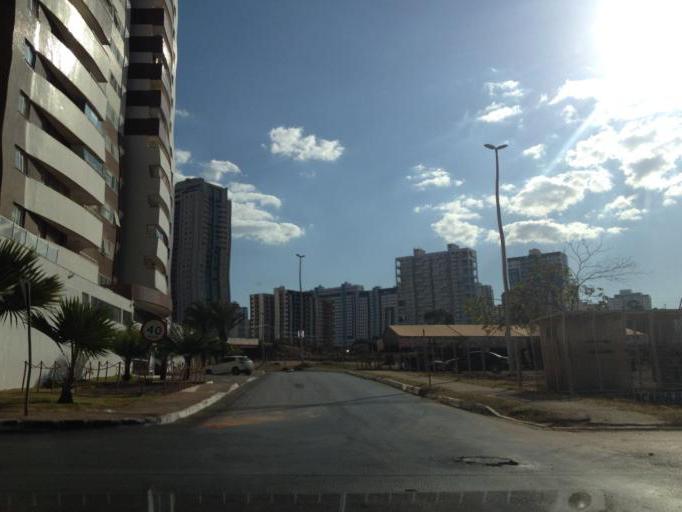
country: BR
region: Federal District
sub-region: Brasilia
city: Brasilia
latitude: -15.8408
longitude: -48.0307
